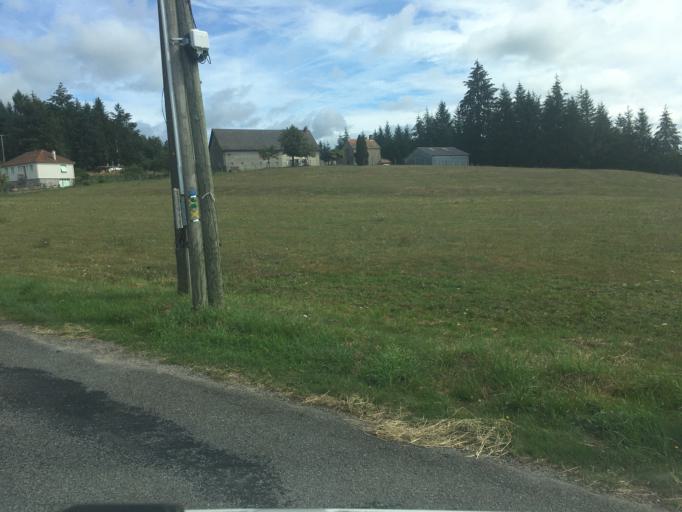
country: FR
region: Auvergne
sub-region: Departement du Cantal
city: Champagnac
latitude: 45.4288
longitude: 2.4136
